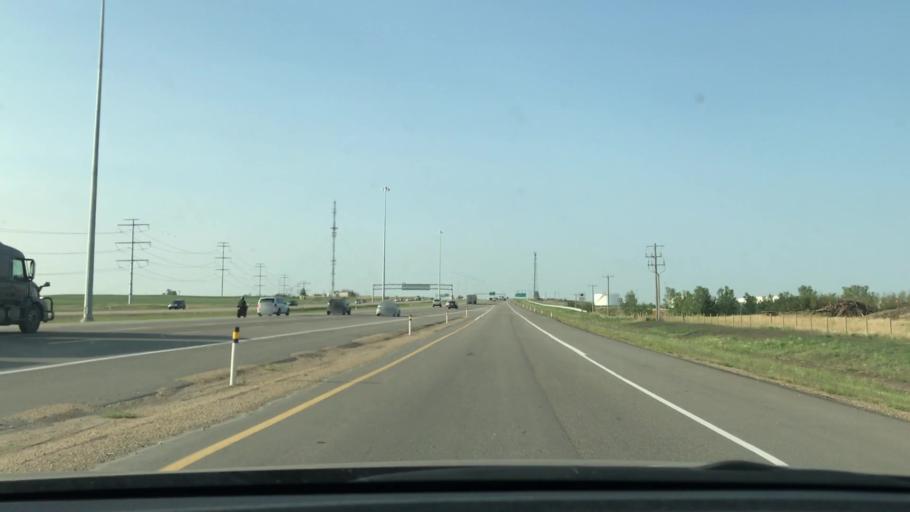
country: CA
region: Alberta
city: Sherwood Park
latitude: 53.5365
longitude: -113.3438
